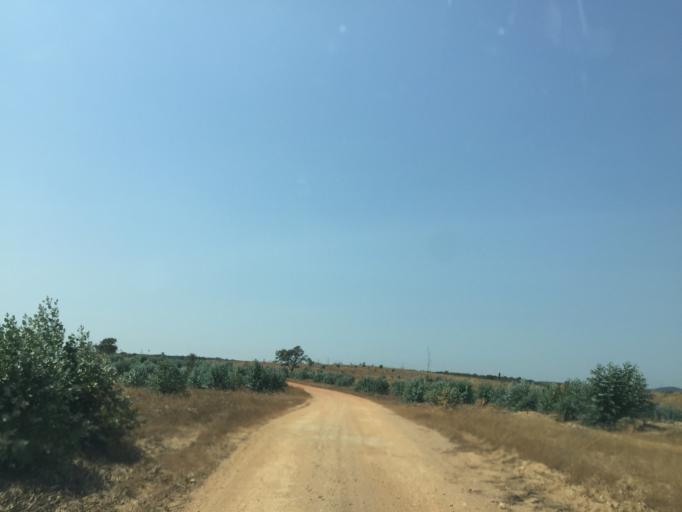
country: PT
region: Setubal
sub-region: Grandola
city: Grandola
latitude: 38.0459
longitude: -8.4551
